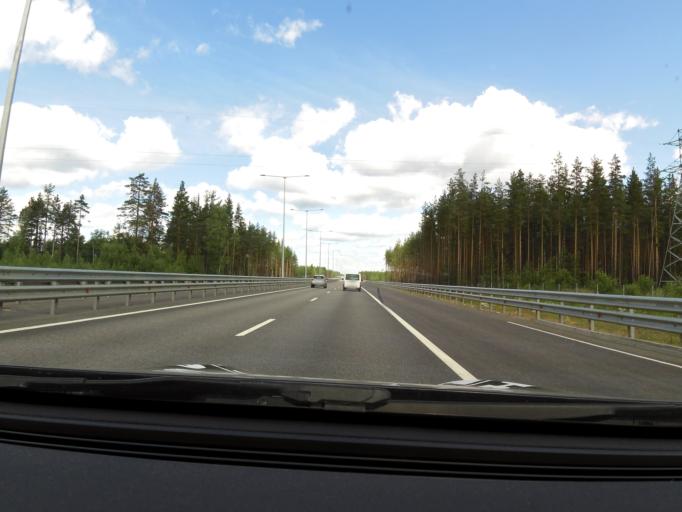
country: RU
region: Tverskaya
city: Krasnomayskiy
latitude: 57.5583
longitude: 34.2664
